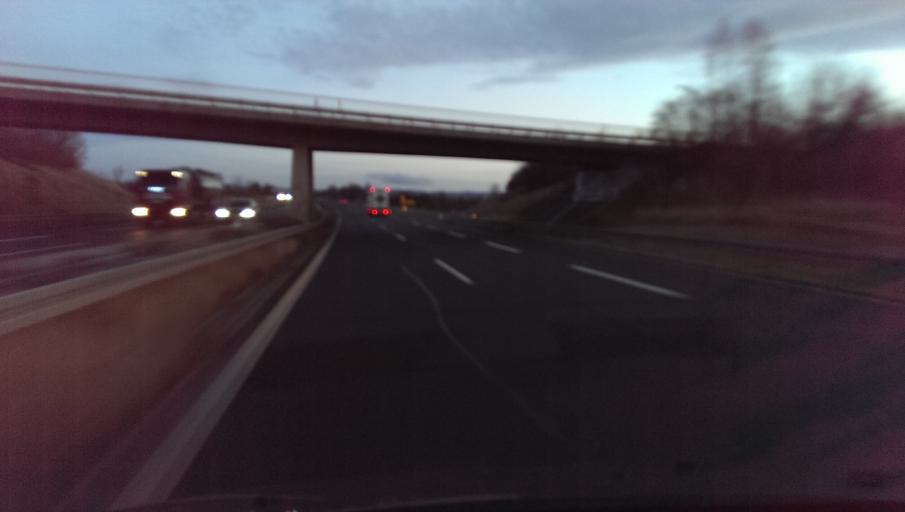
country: DE
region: Saxony-Anhalt
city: Veckenstedt
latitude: 51.8886
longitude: 10.7134
